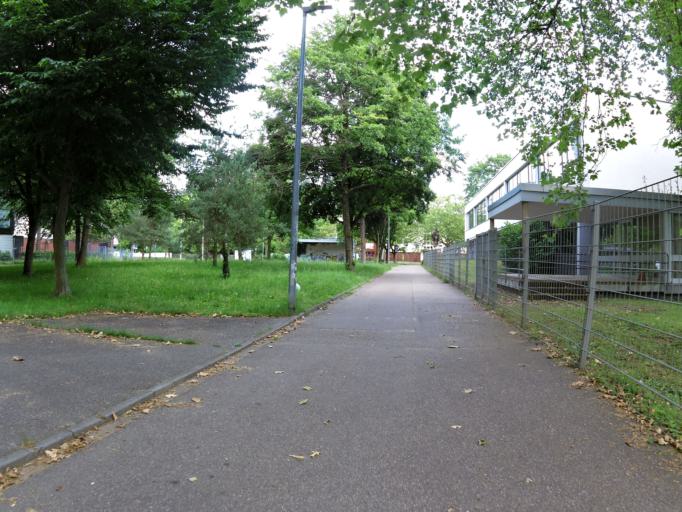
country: DE
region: Baden-Wuerttemberg
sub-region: Freiburg Region
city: Lahr
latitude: 48.3369
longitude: 7.8519
